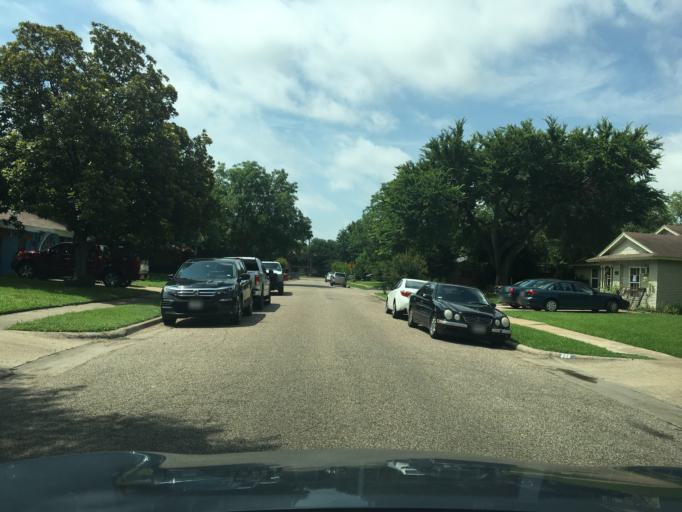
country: US
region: Texas
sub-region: Dallas County
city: Garland
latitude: 32.9181
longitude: -96.6734
